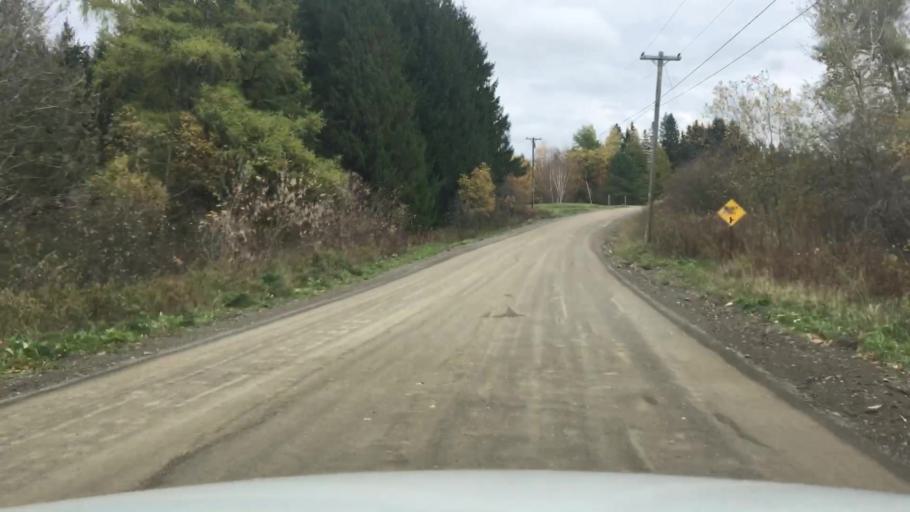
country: US
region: Maine
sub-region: Aroostook County
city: Easton
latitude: 46.5217
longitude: -67.8895
